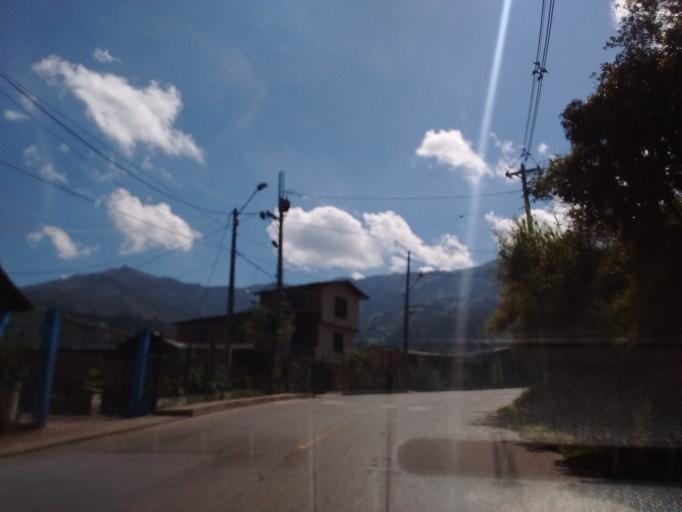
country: CO
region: Antioquia
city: Medellin
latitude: 6.2279
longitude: -75.5305
